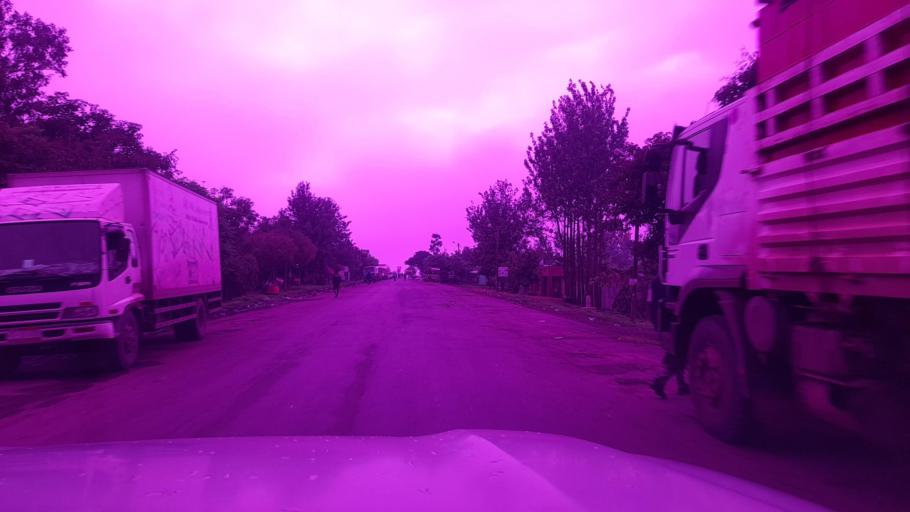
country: ET
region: Oromiya
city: Waliso
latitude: 8.1746
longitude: 37.5728
